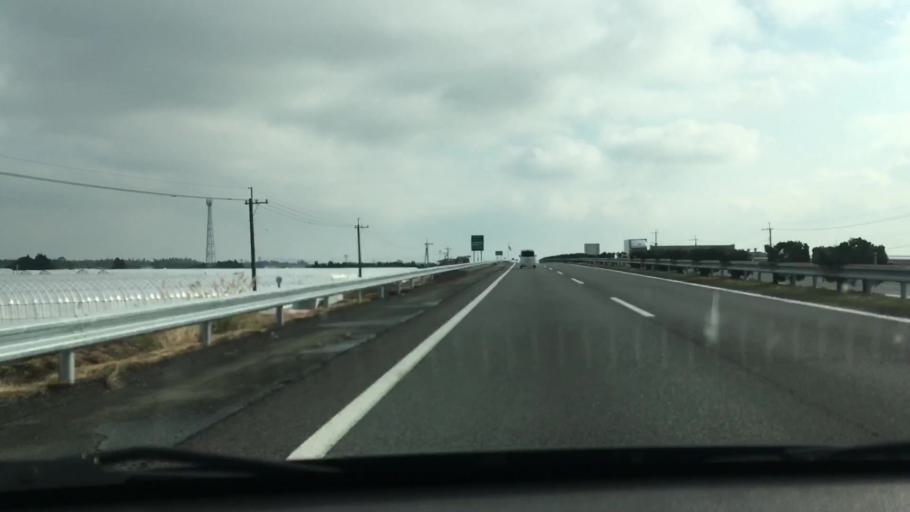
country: JP
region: Kumamoto
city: Ueki
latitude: 32.8907
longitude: 130.7215
